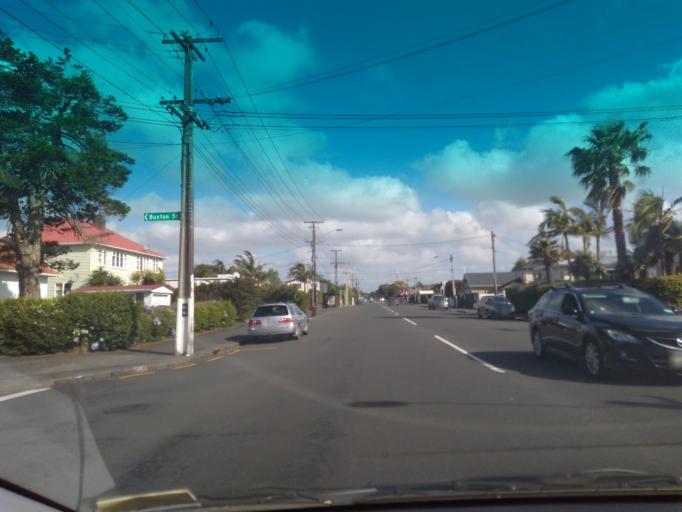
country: NZ
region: Auckland
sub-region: Auckland
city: Rosebank
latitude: -36.8619
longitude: 174.7038
